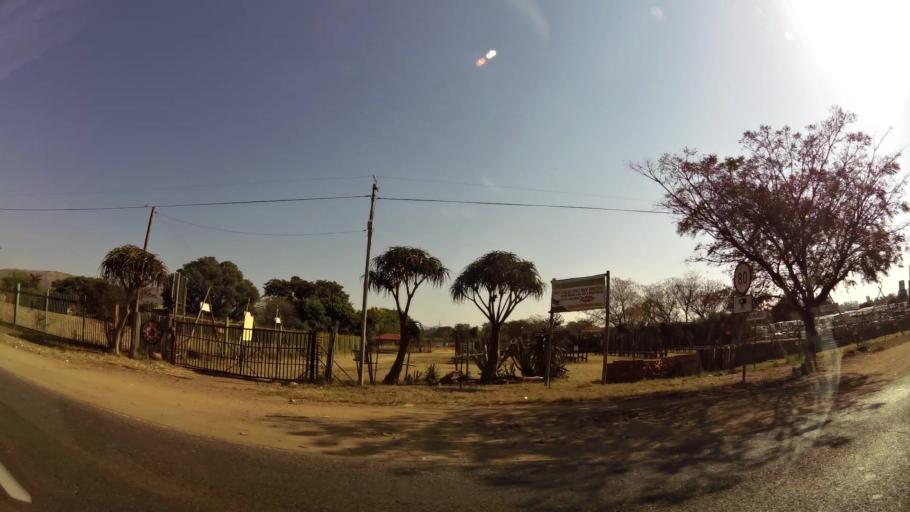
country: ZA
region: Gauteng
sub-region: City of Tshwane Metropolitan Municipality
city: Pretoria
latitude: -25.6677
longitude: 28.1930
